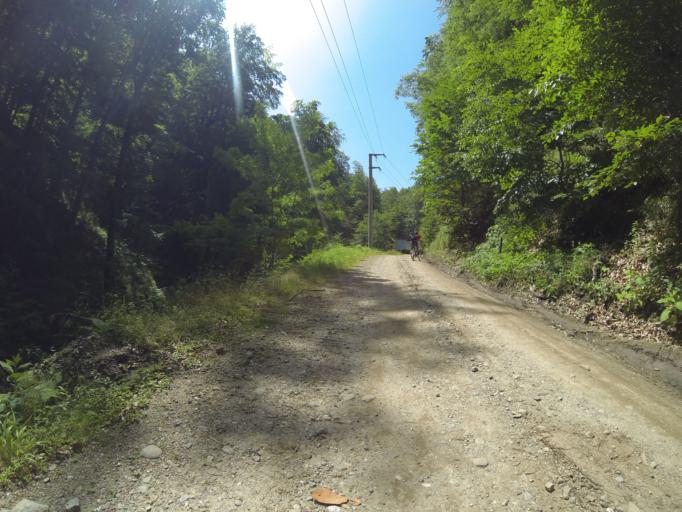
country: RO
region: Valcea
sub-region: Oras Baile Olanesti
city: Baile Olanesti
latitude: 45.2098
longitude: 24.2152
